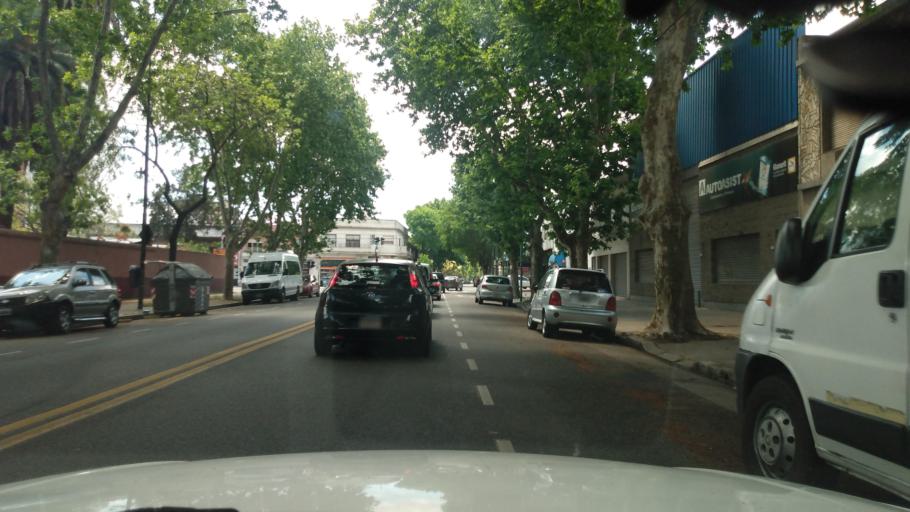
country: AR
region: Buenos Aires
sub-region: Partido de General San Martin
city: General San Martin
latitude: -34.5741
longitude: -58.5037
